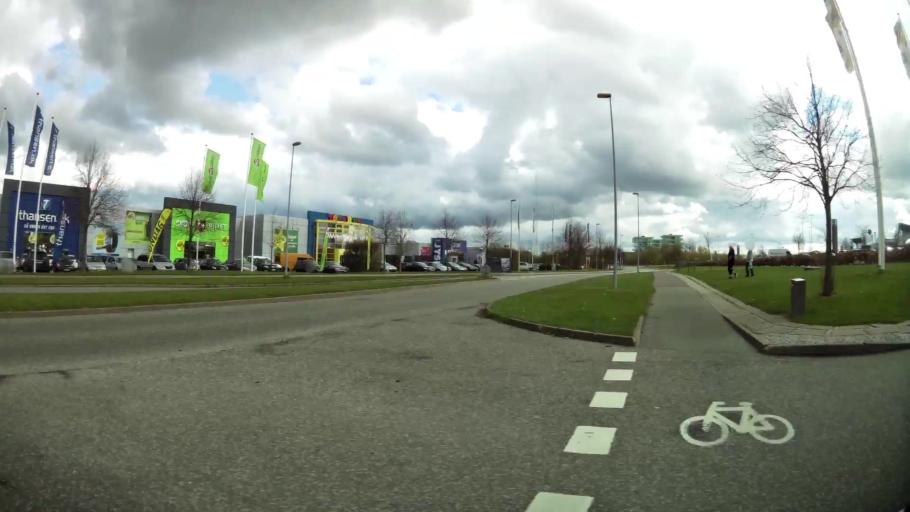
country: DK
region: South Denmark
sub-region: Kolding Kommune
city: Kolding
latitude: 55.5159
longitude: 9.4605
